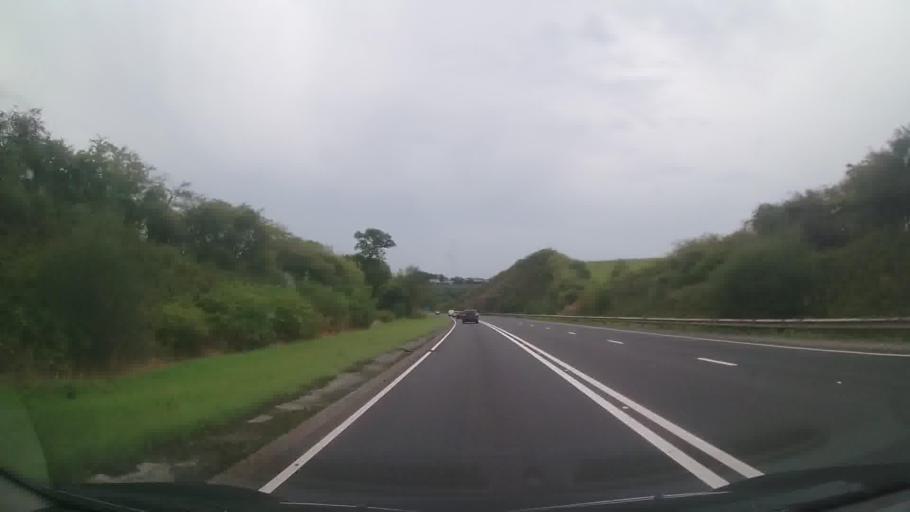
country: GB
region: Wales
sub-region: Pembrokeshire
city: Kilgetty
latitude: 51.7420
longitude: -4.7012
